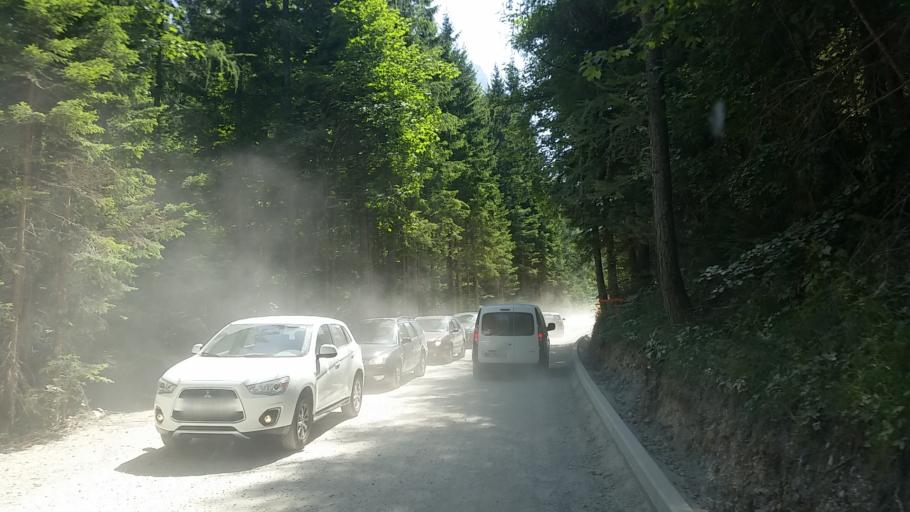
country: SI
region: Kranjska Gora
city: Kranjska Gora
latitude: 46.4424
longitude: 13.7638
